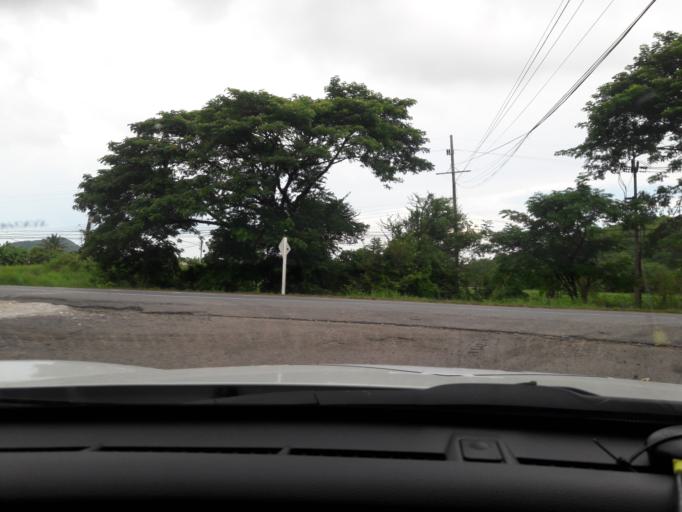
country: TH
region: Nakhon Sawan
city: Tak Fa
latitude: 15.3565
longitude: 100.5024
